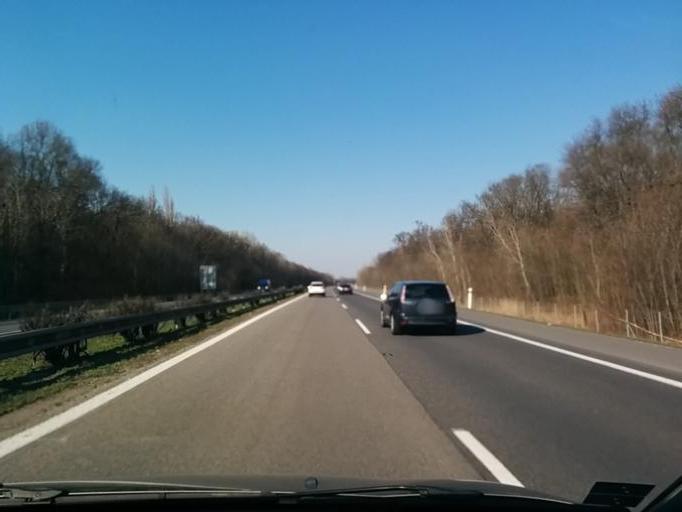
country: SK
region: Trnavsky
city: Leopoldov
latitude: 48.4733
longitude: 17.7438
